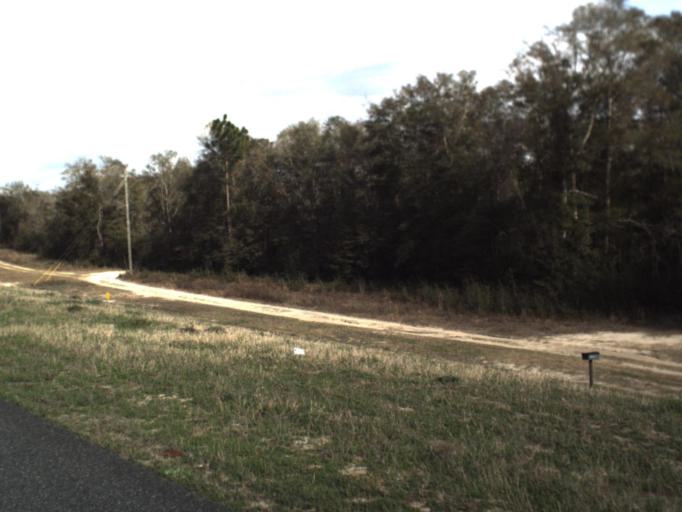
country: US
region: Florida
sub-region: Bay County
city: Youngstown
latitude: 30.5261
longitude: -85.4044
